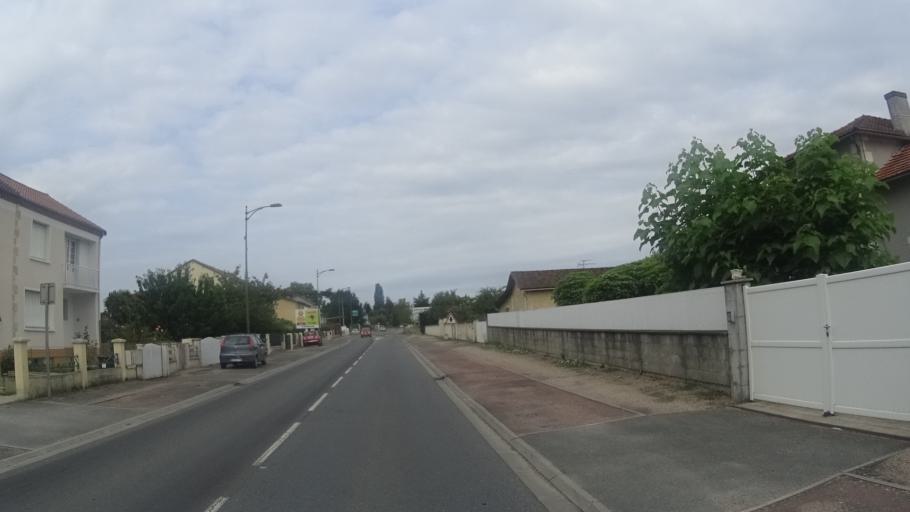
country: FR
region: Aquitaine
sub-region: Departement de la Dordogne
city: Chancelade
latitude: 45.1978
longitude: 0.6592
